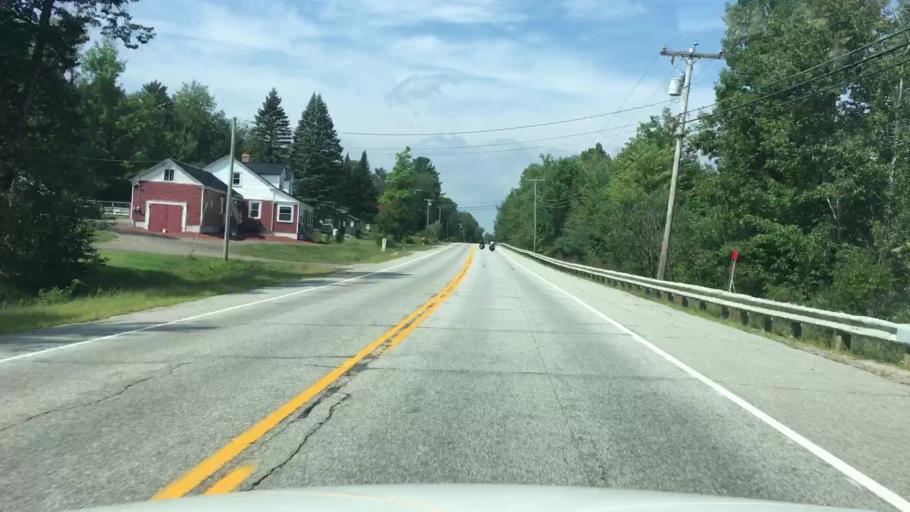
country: US
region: Maine
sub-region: Oxford County
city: Peru
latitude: 44.4951
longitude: -70.3886
